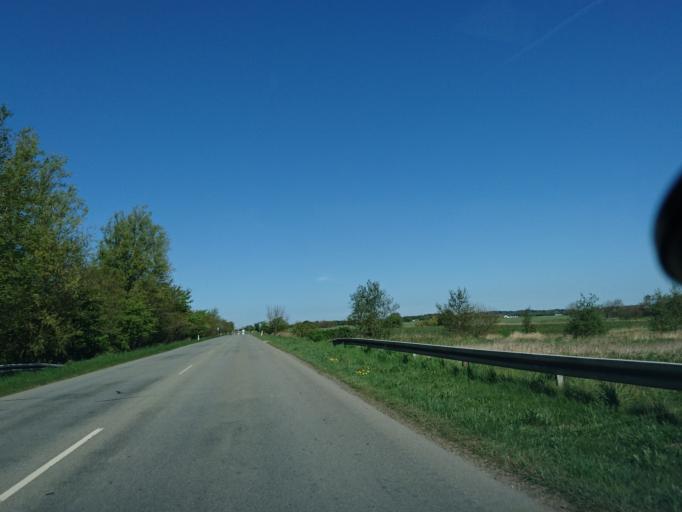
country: DK
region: North Denmark
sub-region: Hjorring Kommune
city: Hjorring
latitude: 57.4657
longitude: 10.0172
